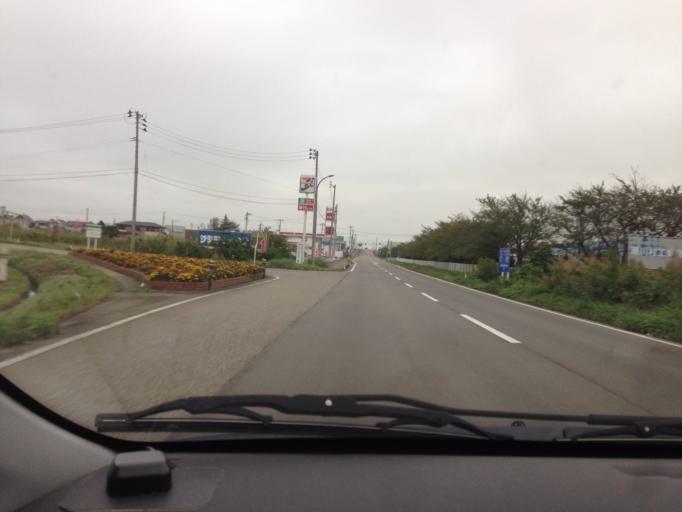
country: JP
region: Fukushima
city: Kitakata
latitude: 37.5849
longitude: 139.8929
